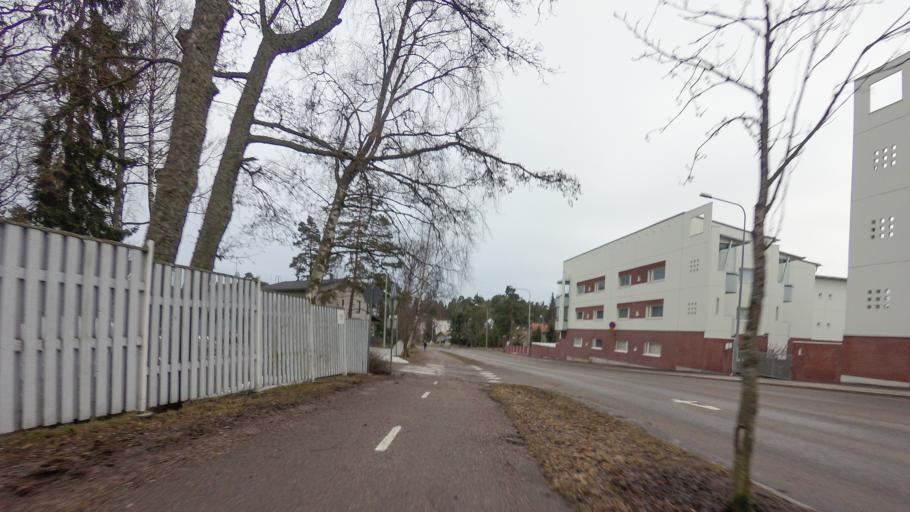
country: FI
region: Uusimaa
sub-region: Helsinki
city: Helsinki
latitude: 60.1638
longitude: 25.0472
